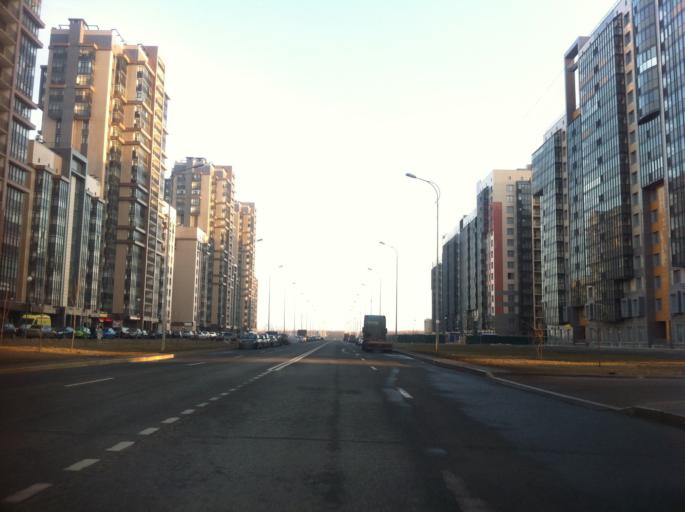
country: RU
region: St.-Petersburg
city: Sosnovaya Polyana
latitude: 59.8508
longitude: 30.1472
